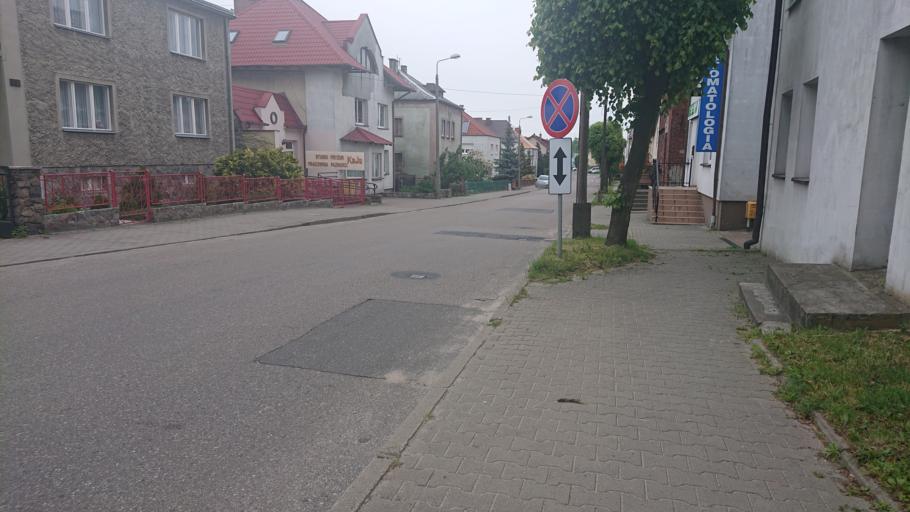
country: PL
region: Pomeranian Voivodeship
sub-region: Powiat chojnicki
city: Chojnice
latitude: 53.6978
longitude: 17.5658
